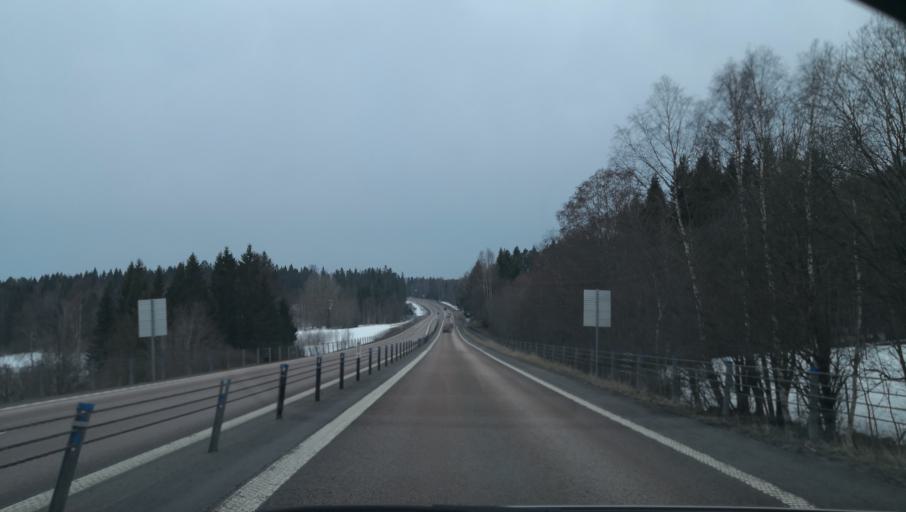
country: SE
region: Vaesternorrland
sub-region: Timra Kommun
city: Soraker
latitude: 62.5626
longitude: 17.7176
